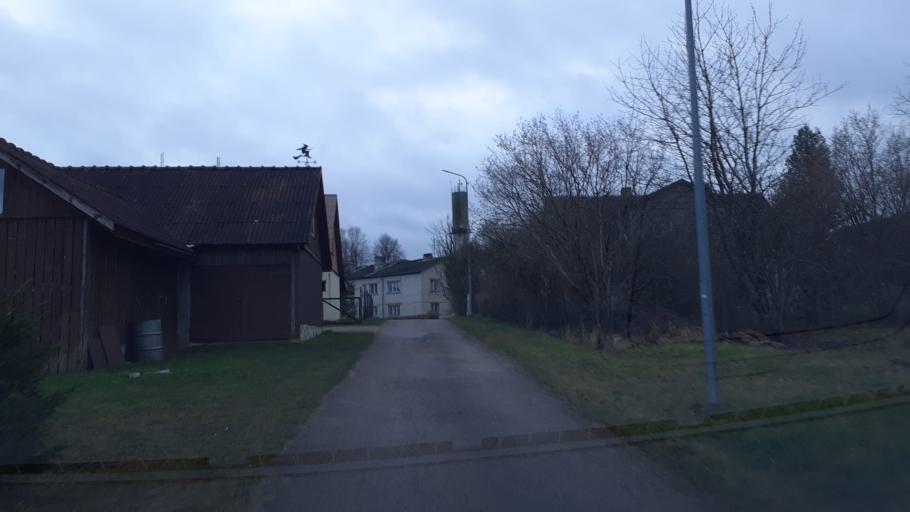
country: LV
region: Talsu Rajons
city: Stende
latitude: 57.0675
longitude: 22.2884
